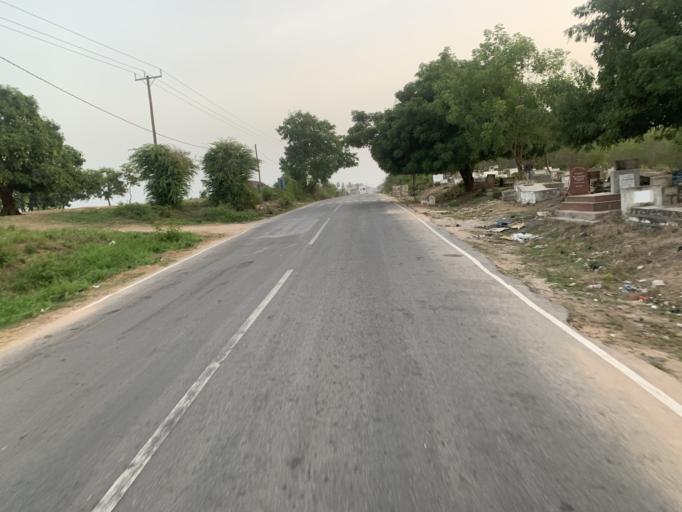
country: GH
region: Central
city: Winneba
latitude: 5.3599
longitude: -0.6097
